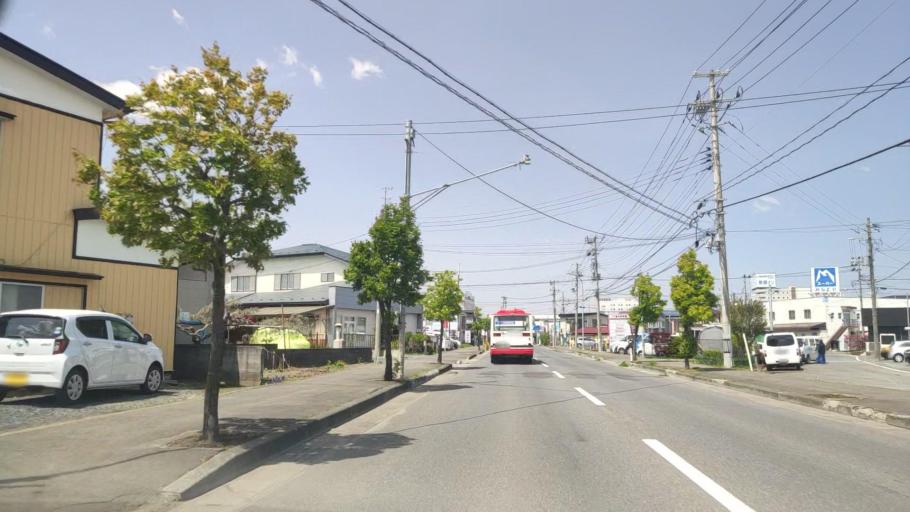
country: JP
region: Aomori
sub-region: Hachinohe Shi
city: Uchimaru
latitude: 40.5064
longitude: 141.4373
